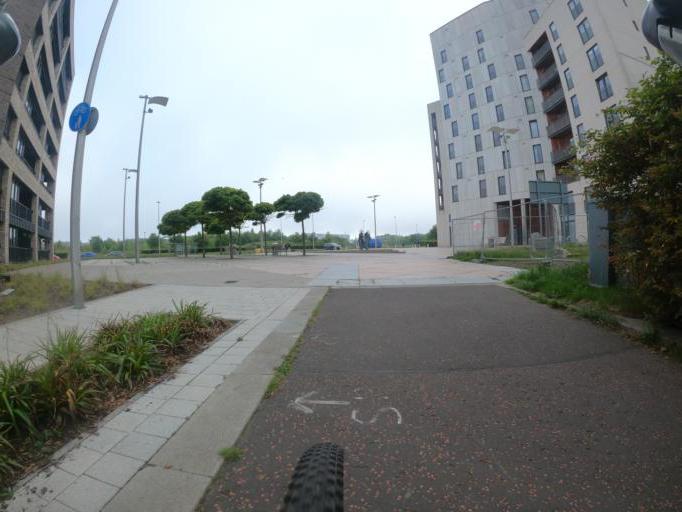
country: GB
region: Scotland
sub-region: Edinburgh
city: Edinburgh
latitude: 55.9815
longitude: -3.2360
